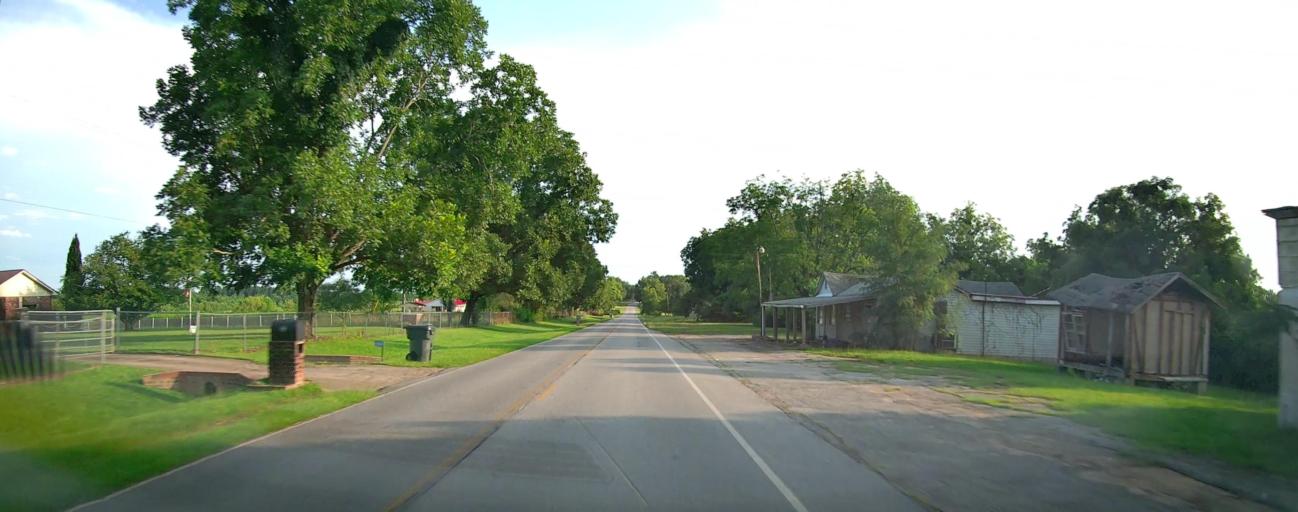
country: US
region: Georgia
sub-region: Peach County
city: Byron
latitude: 32.6833
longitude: -83.8577
